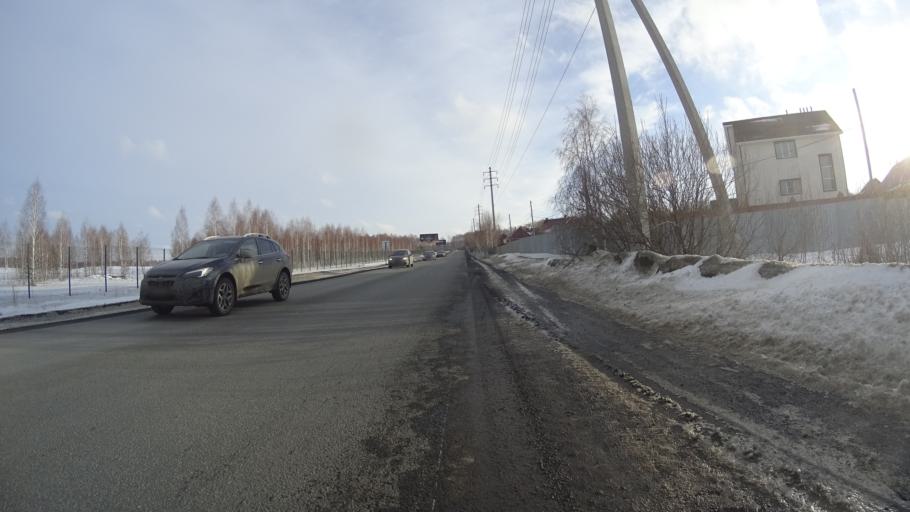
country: RU
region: Chelyabinsk
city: Sargazy
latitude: 55.1327
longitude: 61.2865
